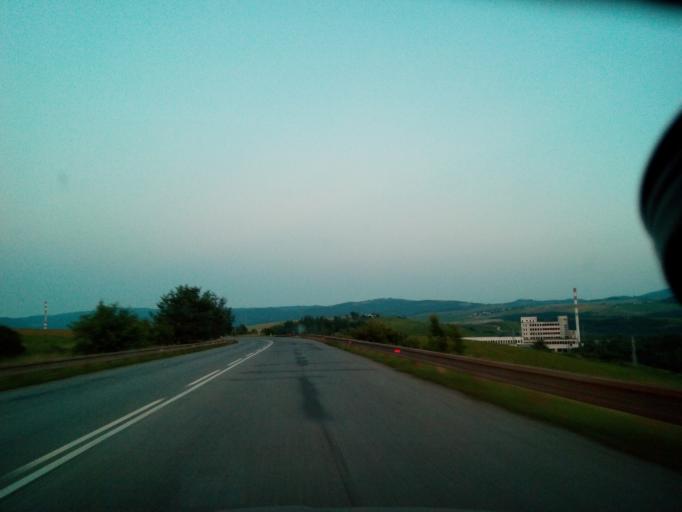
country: SK
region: Kosicky
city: Spisska Nova Ves
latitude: 48.9415
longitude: 20.5856
